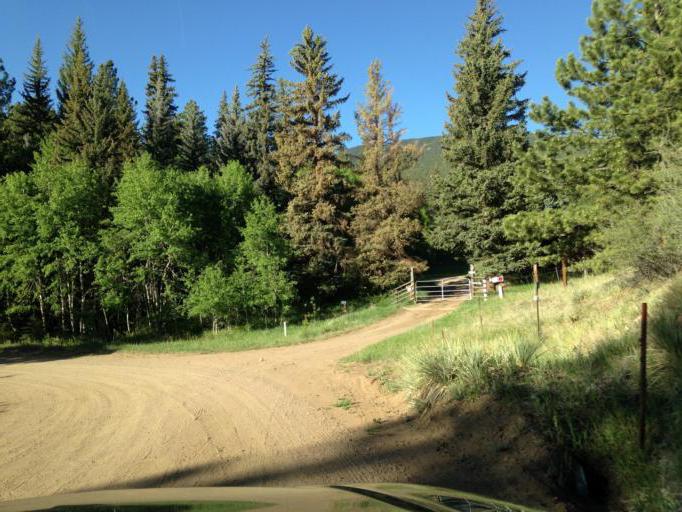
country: US
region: Colorado
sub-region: Jefferson County
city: Evergreen
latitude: 39.4131
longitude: -105.5352
